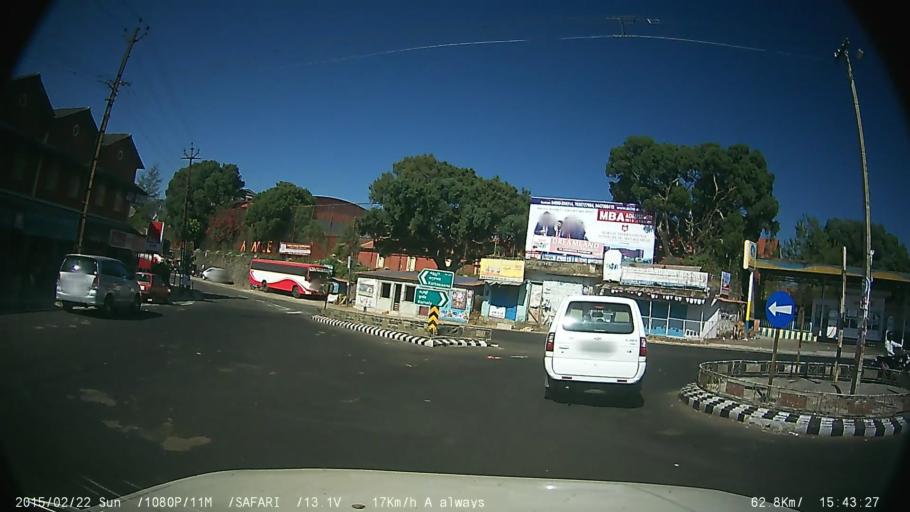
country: IN
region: Kerala
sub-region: Kottayam
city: Erattupetta
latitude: 9.5824
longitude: 76.9709
